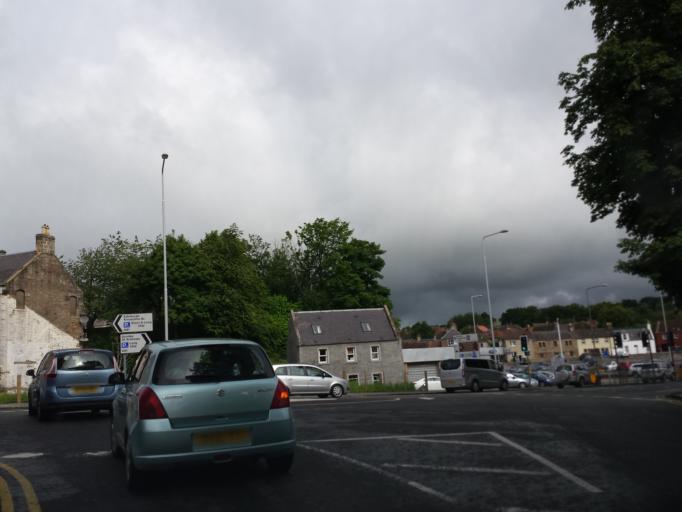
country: GB
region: Scotland
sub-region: Fife
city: Cupar
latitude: 56.3194
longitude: -3.0090
